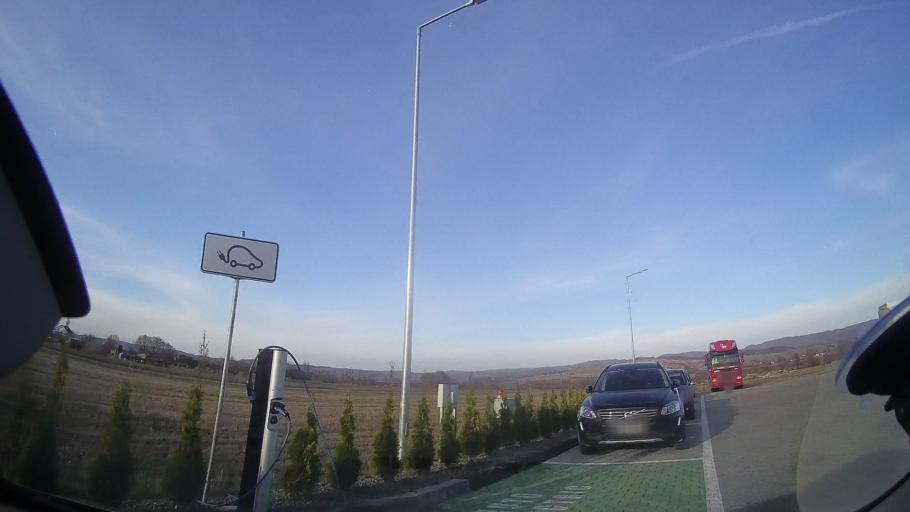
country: RO
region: Bihor
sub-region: Comuna Astileu
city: Astileu
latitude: 47.0413
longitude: 22.3640
